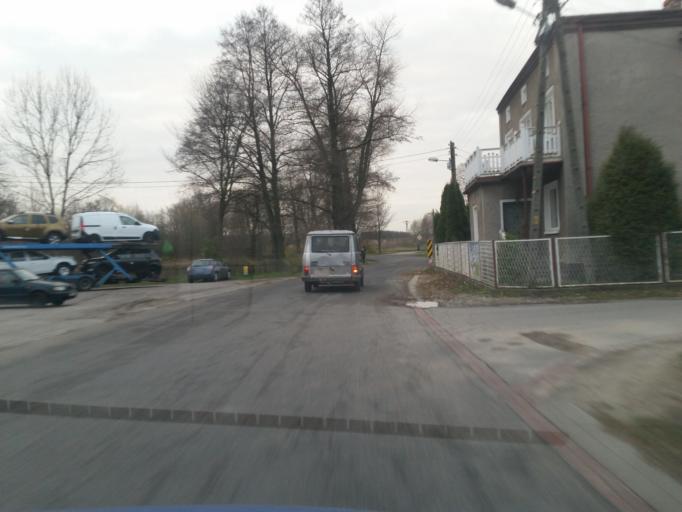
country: PL
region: Silesian Voivodeship
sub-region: Powiat czestochowski
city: Borowno
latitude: 50.9659
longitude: 19.2767
